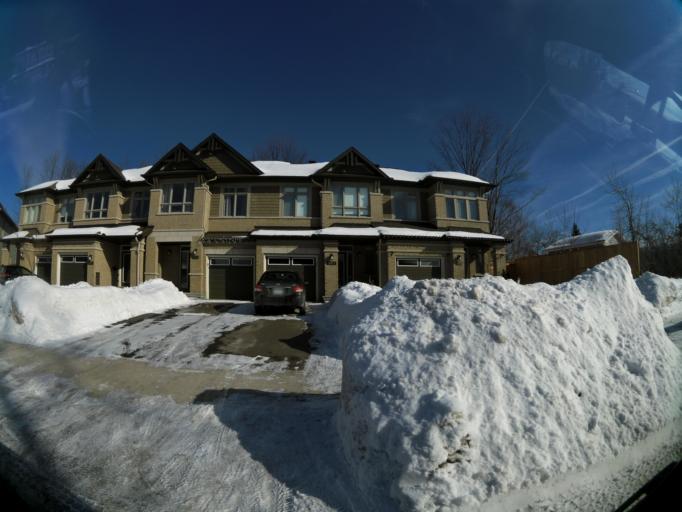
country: CA
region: Ontario
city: Ottawa
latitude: 45.4328
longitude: -75.5115
